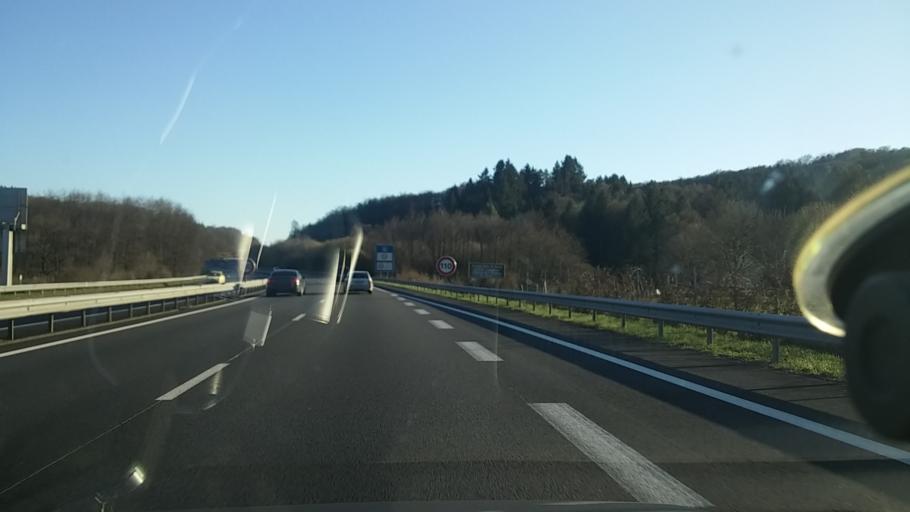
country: FR
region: Limousin
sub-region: Departement de la Haute-Vienne
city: Razes
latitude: 46.0150
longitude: 1.3388
